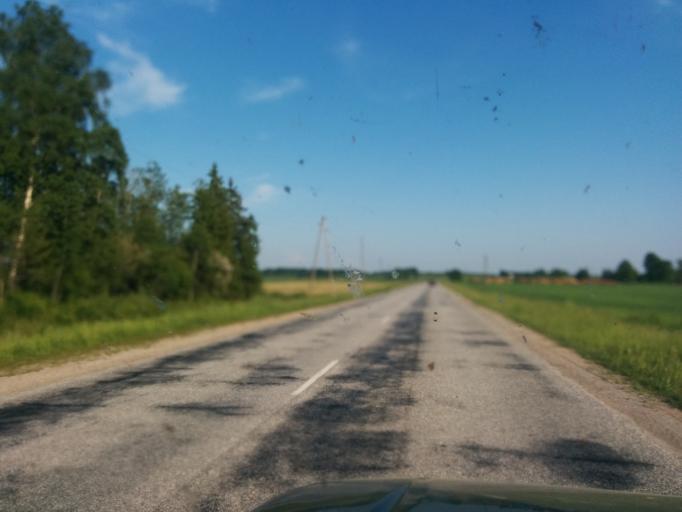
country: LV
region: Talsu Rajons
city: Talsi
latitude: 57.2983
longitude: 22.5607
